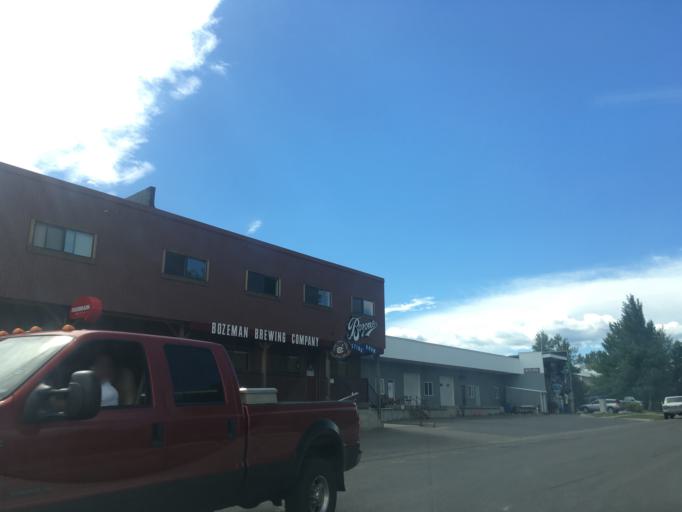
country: US
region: Montana
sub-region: Gallatin County
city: Bozeman
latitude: 45.6848
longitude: -111.0241
